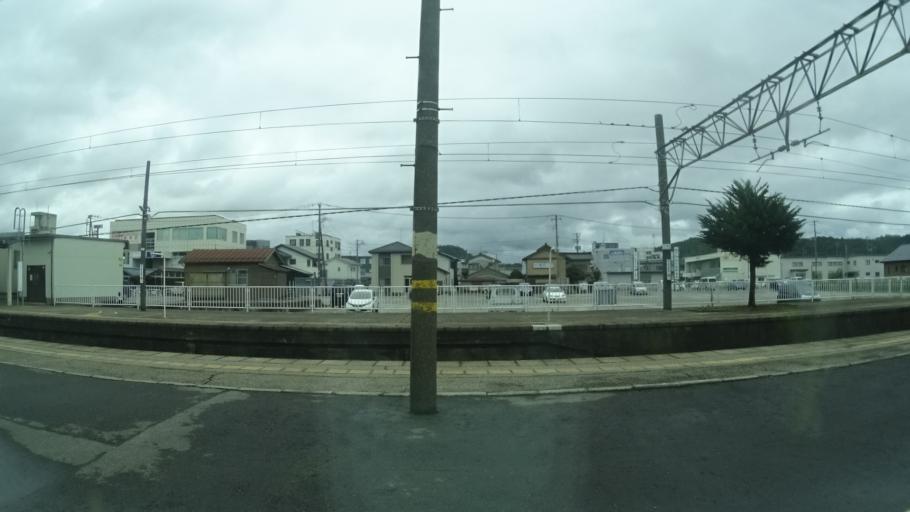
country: JP
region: Niigata
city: Murakami
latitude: 38.2197
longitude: 139.4633
